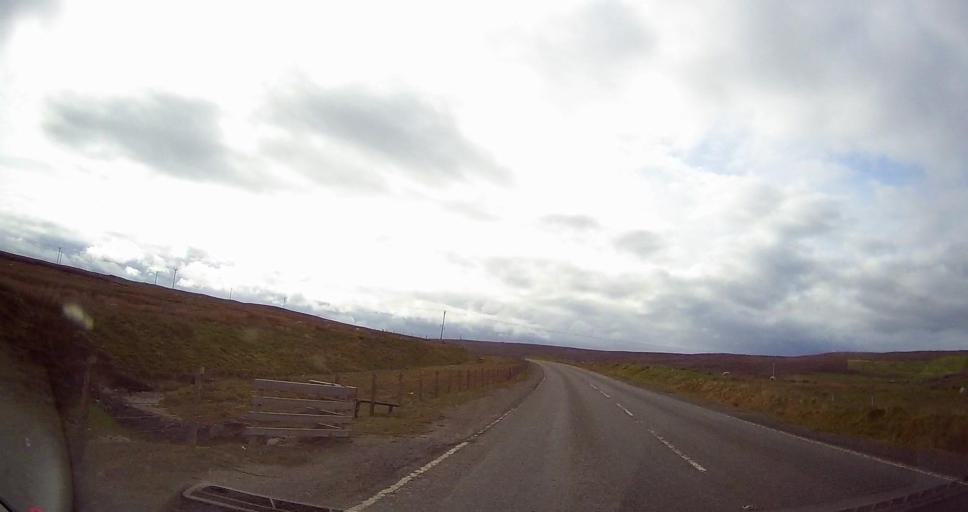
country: GB
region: Scotland
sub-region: Shetland Islands
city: Lerwick
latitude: 60.4468
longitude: -1.2525
